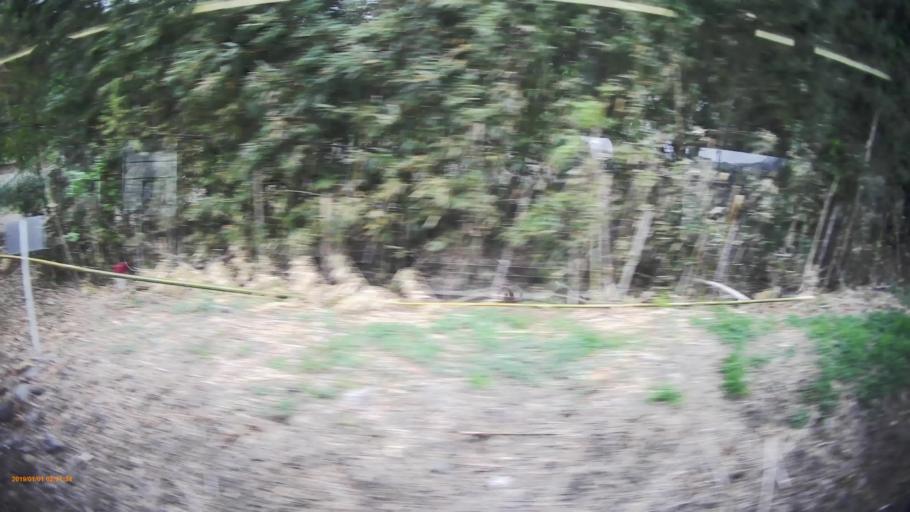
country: JP
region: Yamanashi
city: Ryuo
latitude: 35.6797
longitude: 138.4988
